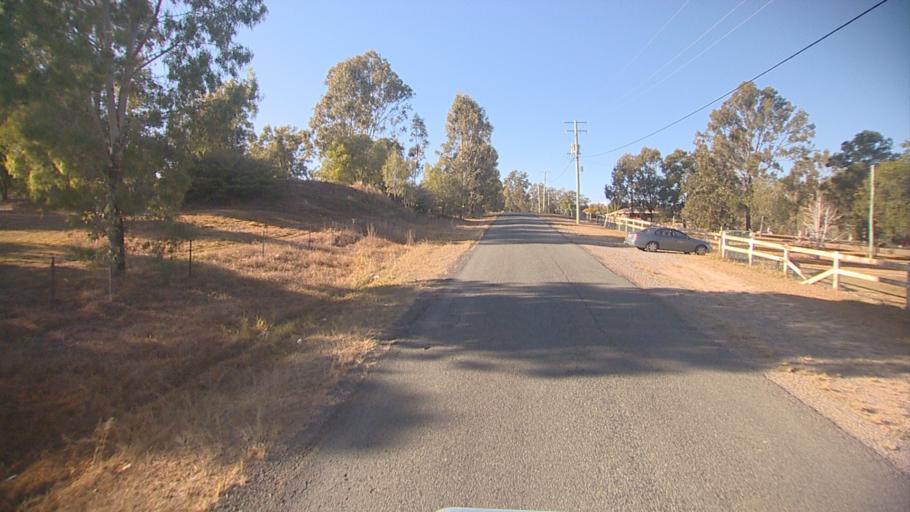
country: AU
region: Queensland
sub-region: Logan
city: Cedar Vale
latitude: -27.8350
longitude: 153.0072
